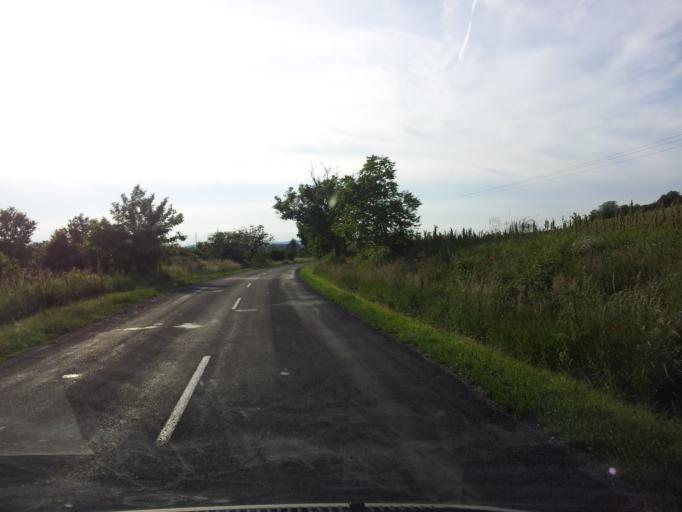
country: HU
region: Komarom-Esztergom
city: Esztergom
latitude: 47.7586
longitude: 18.7682
